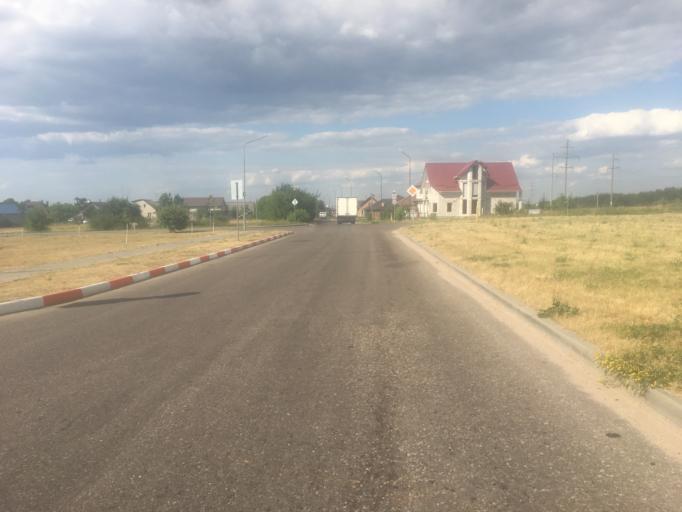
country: BY
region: Grodnenskaya
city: Hrodna
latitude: 53.6474
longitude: 23.8127
